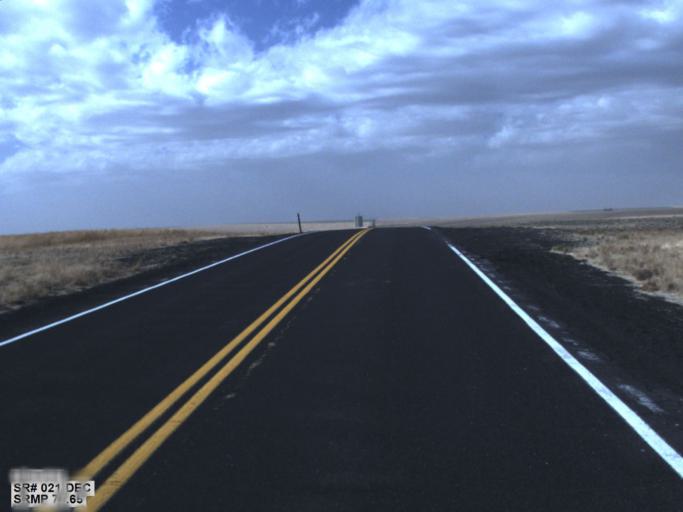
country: US
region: Washington
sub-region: Okanogan County
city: Coulee Dam
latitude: 47.6125
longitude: -118.7525
